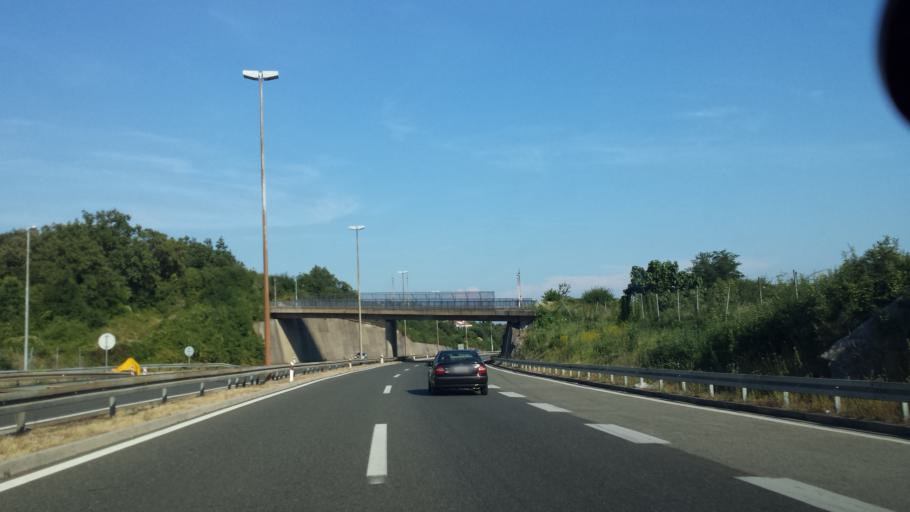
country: HR
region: Primorsko-Goranska
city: Rubesi
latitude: 45.3546
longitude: 14.3549
